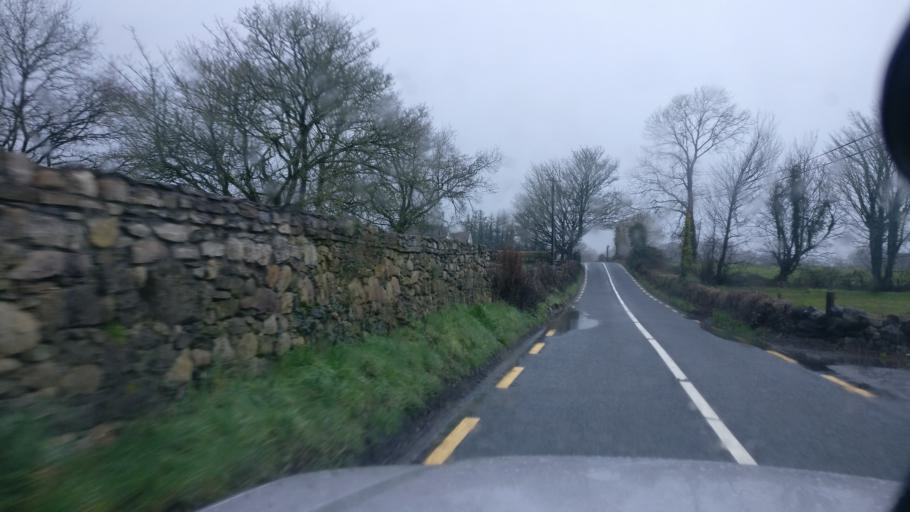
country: IE
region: Connaught
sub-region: County Galway
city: Loughrea
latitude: 53.1533
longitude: -8.4780
